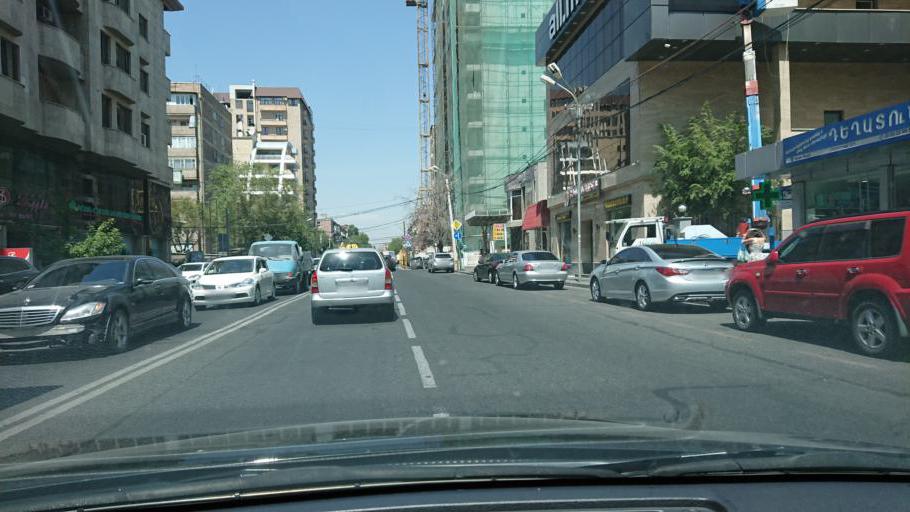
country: AM
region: Yerevan
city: Yerevan
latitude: 40.1992
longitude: 44.5013
